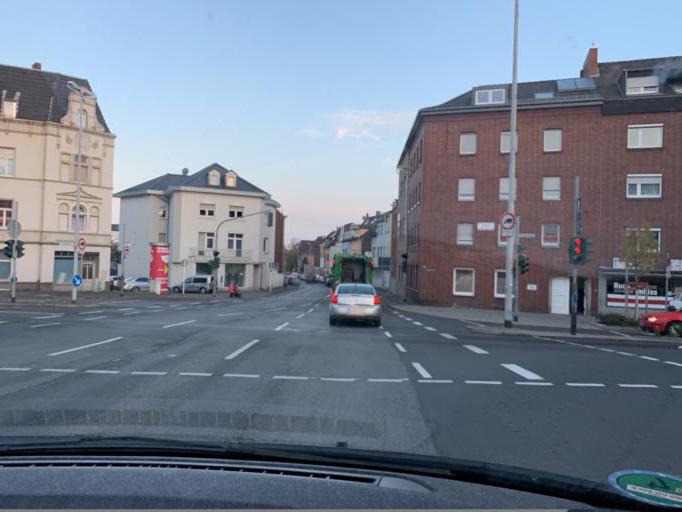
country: DE
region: North Rhine-Westphalia
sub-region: Regierungsbezirk Dusseldorf
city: Monchengladbach
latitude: 51.1323
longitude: 6.4505
